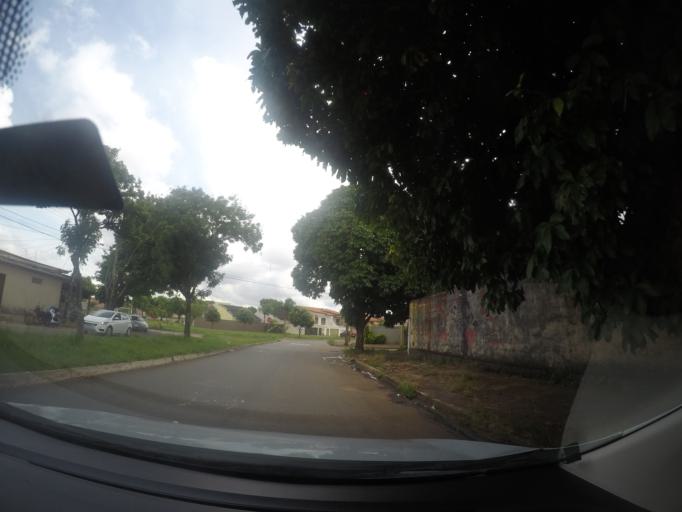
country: BR
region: Goias
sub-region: Goiania
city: Goiania
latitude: -16.7161
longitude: -49.3041
